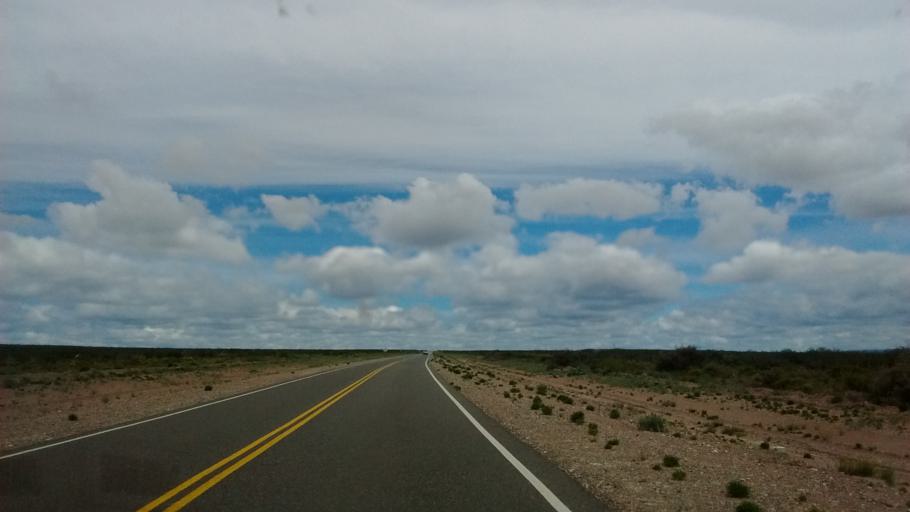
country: AR
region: Neuquen
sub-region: Departamento de Picun Leufu
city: Picun Leufu
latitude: -39.7485
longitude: -69.6189
